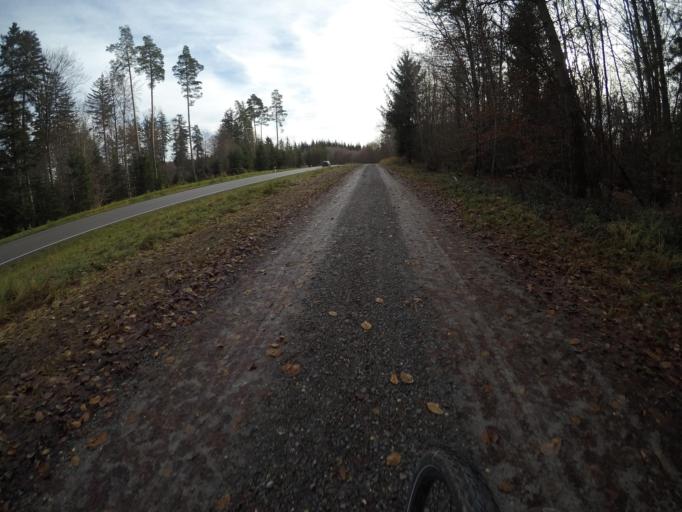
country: DE
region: Baden-Wuerttemberg
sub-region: Regierungsbezirk Stuttgart
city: Winterbach
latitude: 48.7700
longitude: 9.4757
